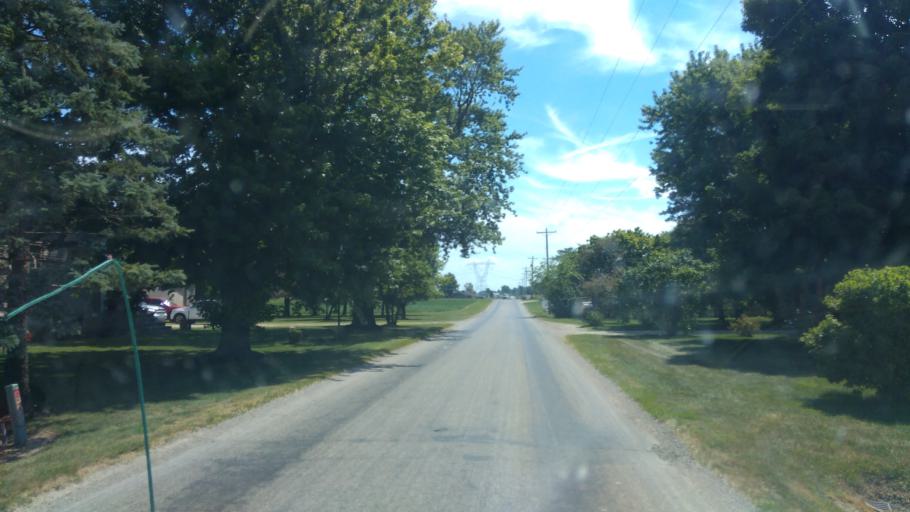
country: US
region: Indiana
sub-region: Adams County
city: Berne
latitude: 40.7012
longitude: -84.9655
